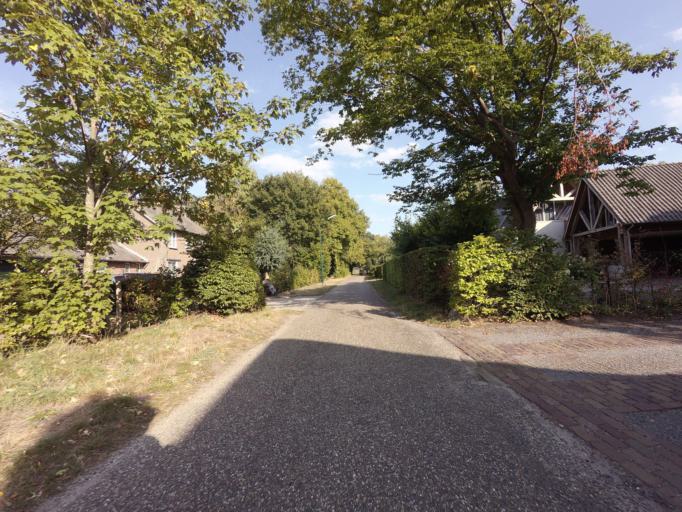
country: NL
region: North Brabant
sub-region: Gemeente Heeze-Leende
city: Heeze
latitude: 51.3590
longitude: 5.5941
